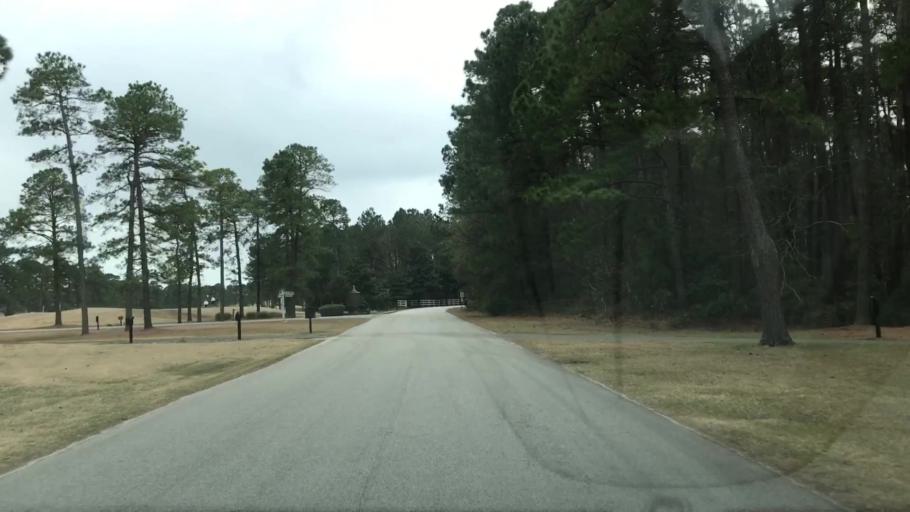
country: US
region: South Carolina
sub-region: Horry County
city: Red Hill
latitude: 33.7743
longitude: -79.0039
